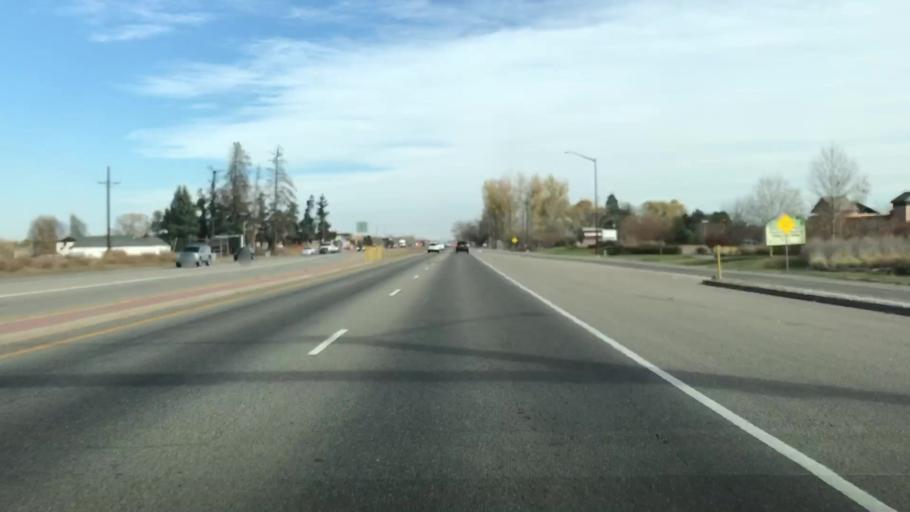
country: US
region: Colorado
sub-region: Larimer County
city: Loveland
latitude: 40.4072
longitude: -105.0349
